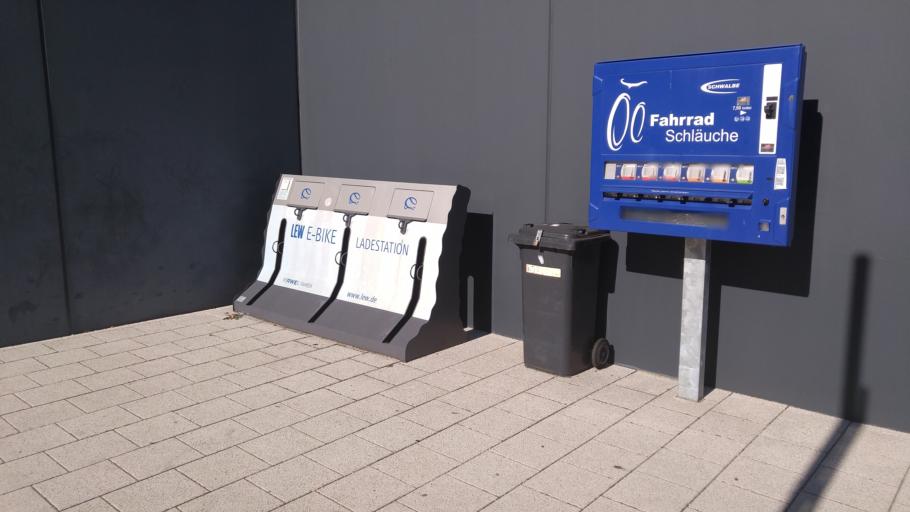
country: DE
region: Bavaria
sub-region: Swabia
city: Guenzburg
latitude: 48.4604
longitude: 10.2799
